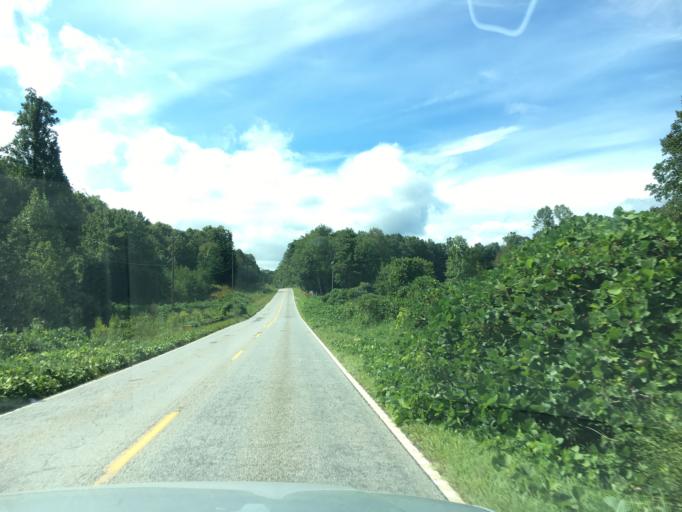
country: US
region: North Carolina
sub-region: Polk County
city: Columbus
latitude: 35.3163
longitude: -82.1737
